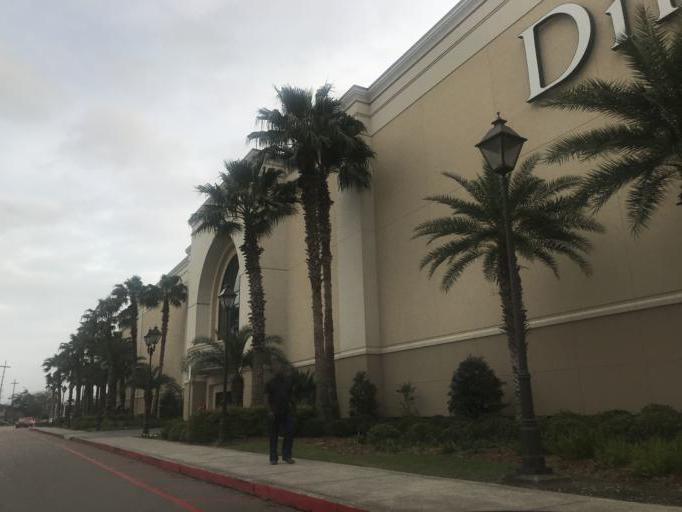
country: US
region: Louisiana
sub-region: Jefferson Parish
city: Metairie
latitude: 30.0077
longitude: -90.1576
